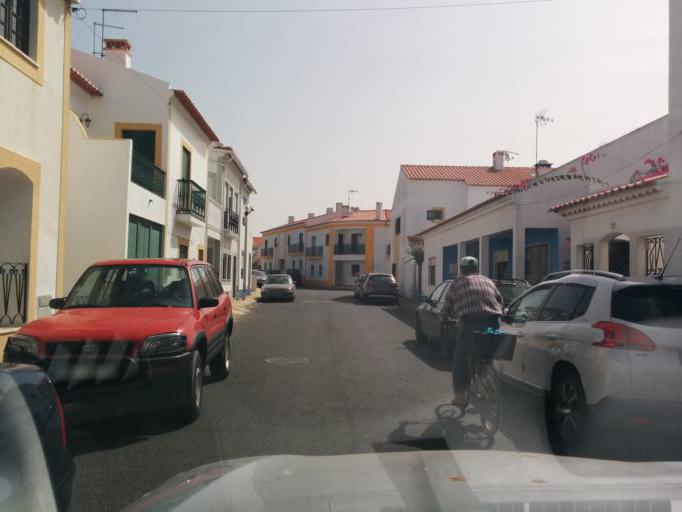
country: PT
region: Beja
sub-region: Odemira
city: Vila Nova de Milfontes
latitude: 37.7292
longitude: -8.7794
